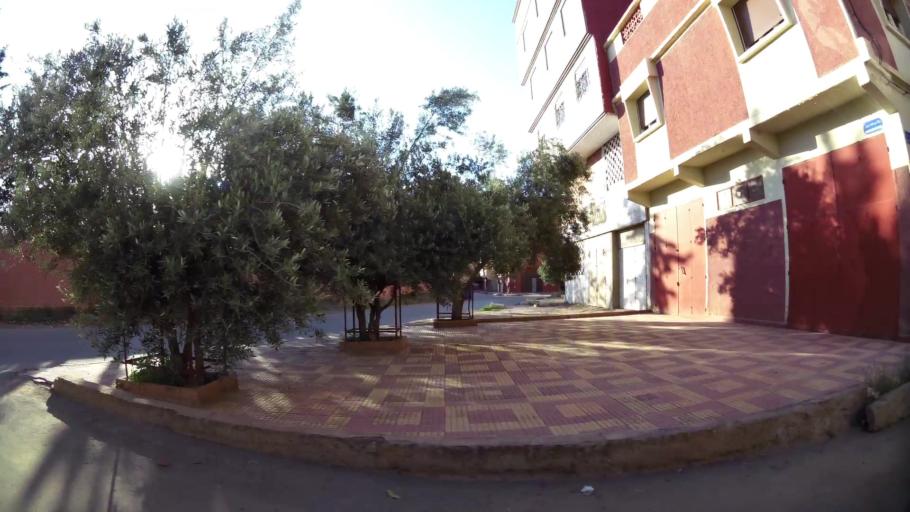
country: MA
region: Oriental
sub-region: Berkane-Taourirt
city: Berkane
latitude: 34.9295
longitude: -2.3262
